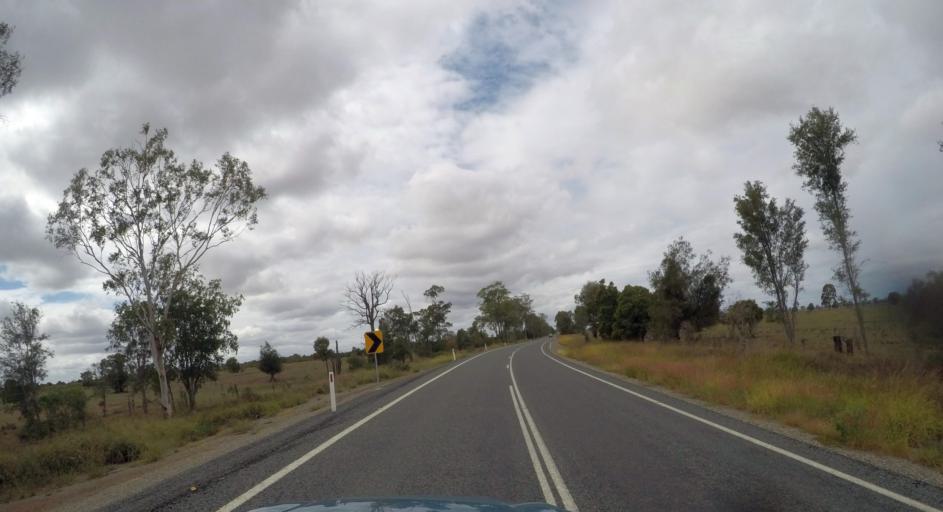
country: AU
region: Queensland
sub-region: South Burnett
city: Kingaroy
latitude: -26.3902
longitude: 151.2024
